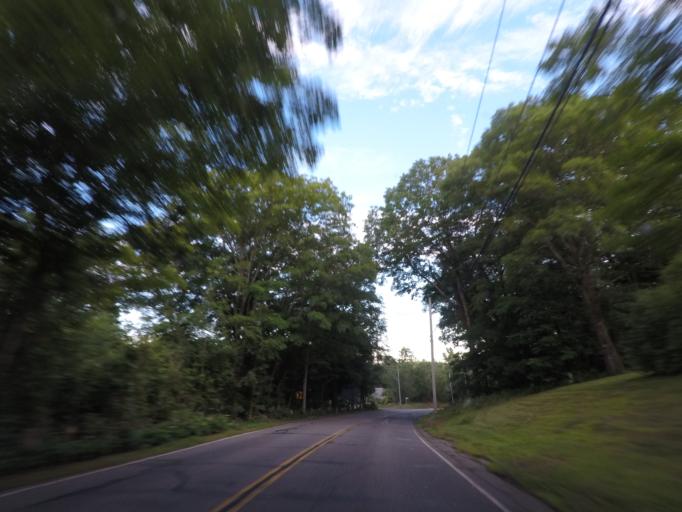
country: US
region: Massachusetts
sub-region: Hampshire County
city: Ware
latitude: 42.2146
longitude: -72.2495
